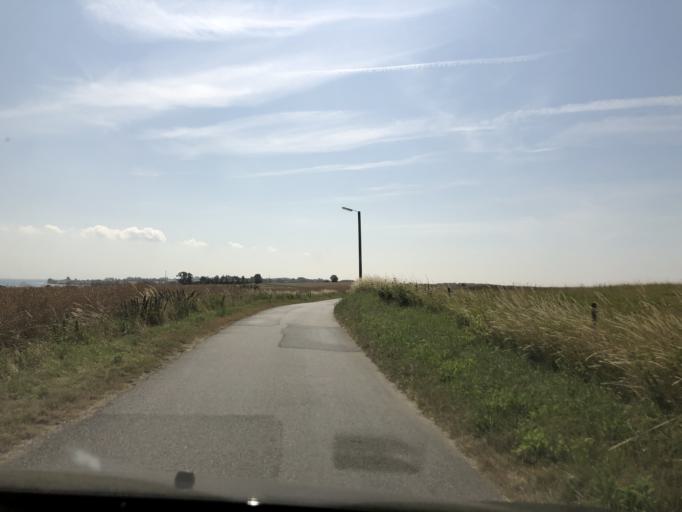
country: DK
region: South Denmark
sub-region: Faaborg-Midtfyn Kommune
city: Faaborg
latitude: 54.9482
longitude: 10.2347
